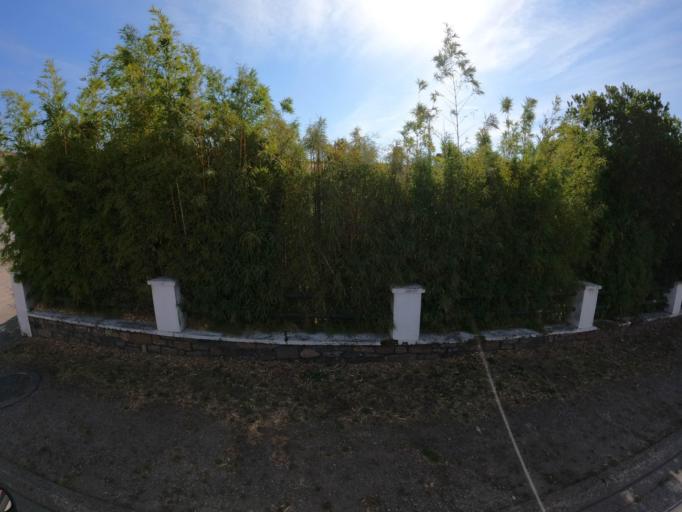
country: FR
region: Pays de la Loire
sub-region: Departement de la Vendee
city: Falleron
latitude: 46.8800
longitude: -1.7038
